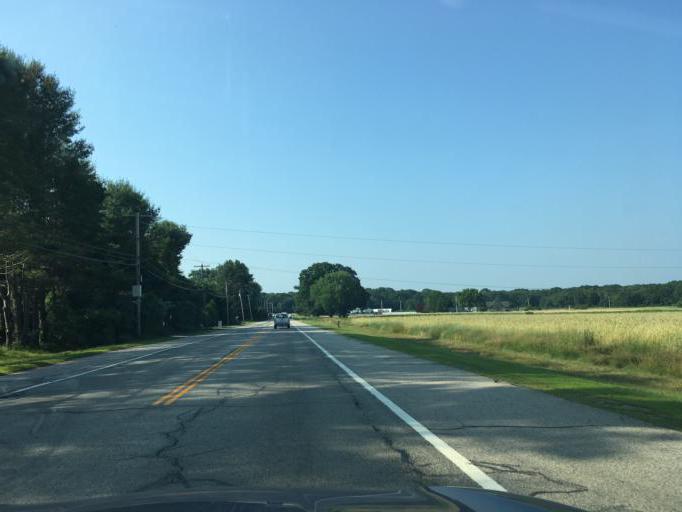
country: US
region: Rhode Island
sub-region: Washington County
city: Exeter
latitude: 41.5628
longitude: -71.5178
